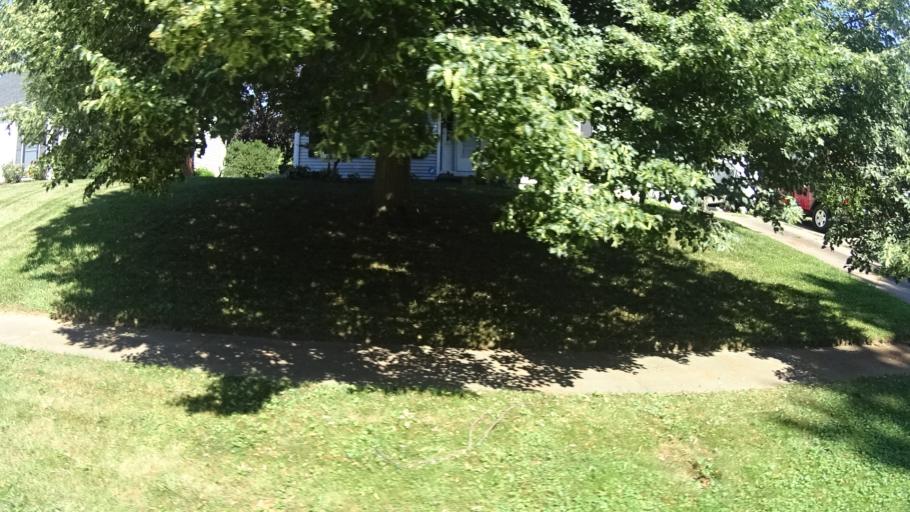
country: US
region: Ohio
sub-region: Erie County
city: Huron
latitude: 41.3799
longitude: -82.5674
